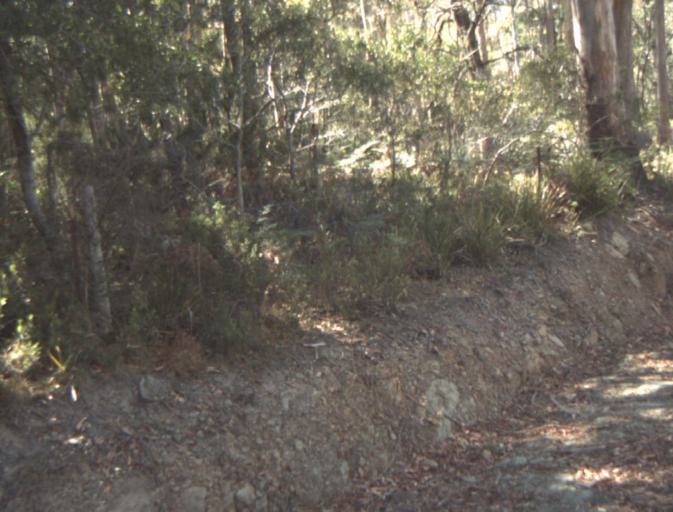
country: AU
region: Tasmania
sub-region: Launceston
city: Newstead
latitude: -41.3248
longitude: 147.3410
